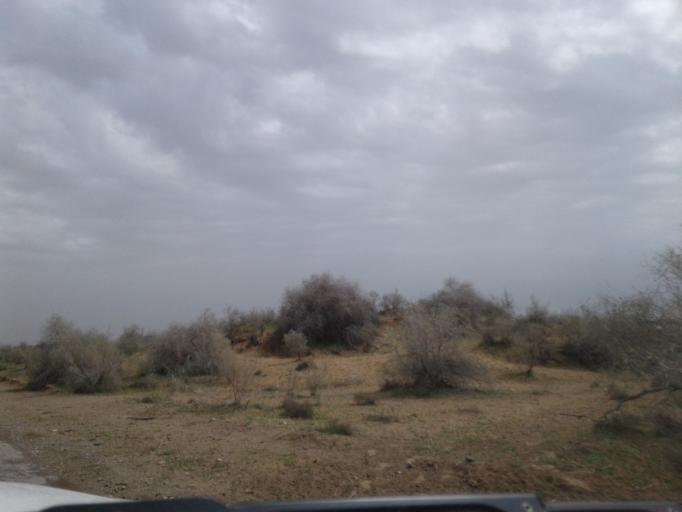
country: TM
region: Lebap
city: Atamyrat
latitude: 38.1700
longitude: 64.9164
